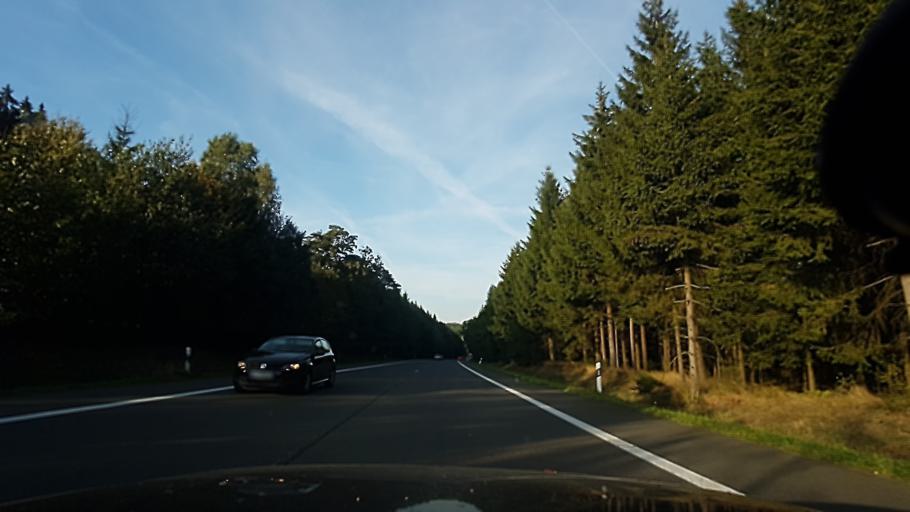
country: DE
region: North Rhine-Westphalia
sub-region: Regierungsbezirk Koln
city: Marienheide
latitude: 51.0833
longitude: 7.5784
